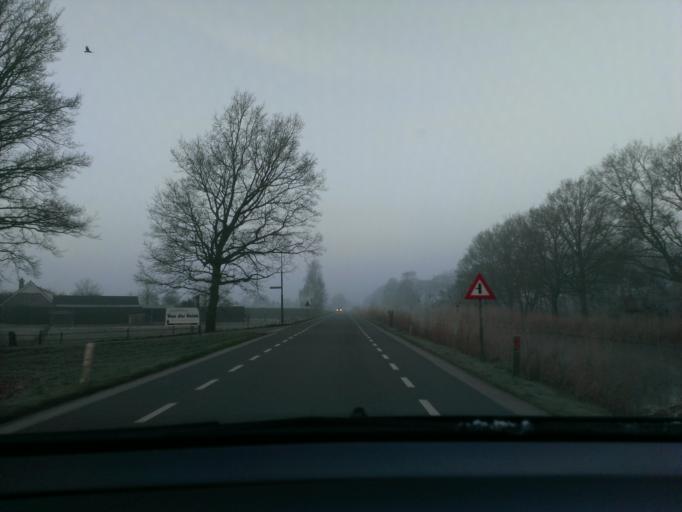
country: NL
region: Gelderland
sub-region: Gemeente Heerde
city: Heerde
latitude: 52.3763
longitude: 6.0455
